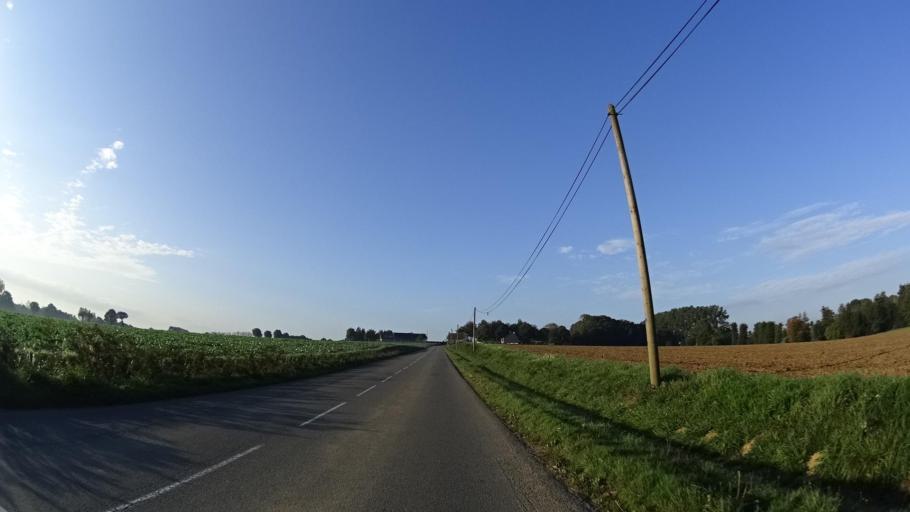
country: FR
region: Brittany
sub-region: Departement d'Ille-et-Vilaine
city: Quedillac
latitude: 48.2469
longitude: -2.1470
